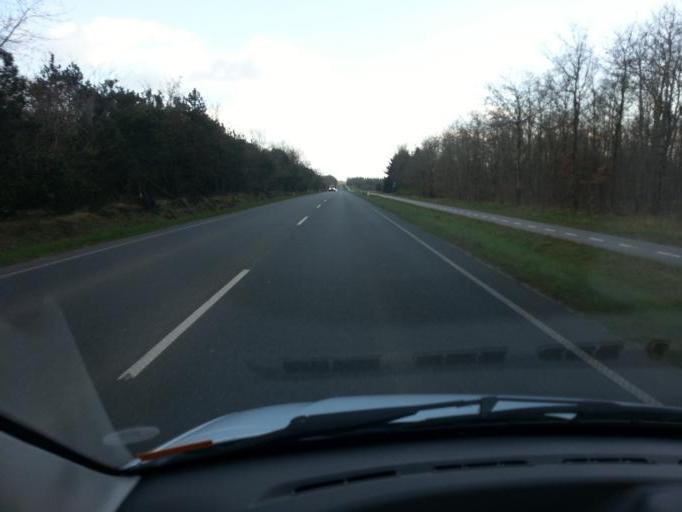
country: DK
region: South Denmark
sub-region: Varde Kommune
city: Varde
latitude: 55.5884
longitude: 8.4933
